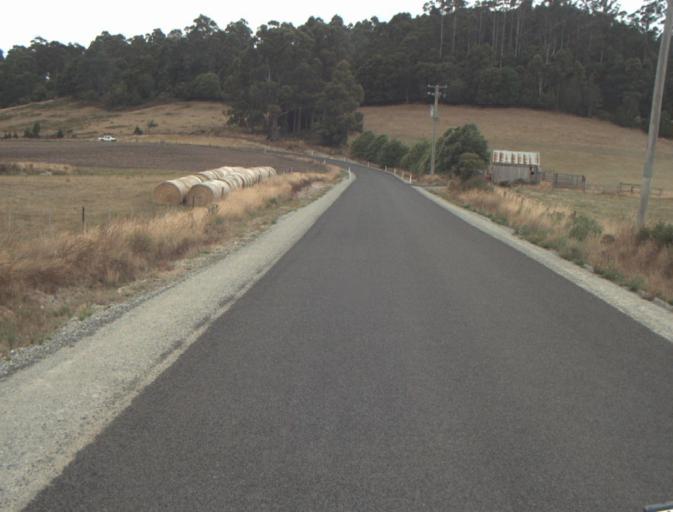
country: AU
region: Tasmania
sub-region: Launceston
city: Mayfield
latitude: -41.2020
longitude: 147.1893
